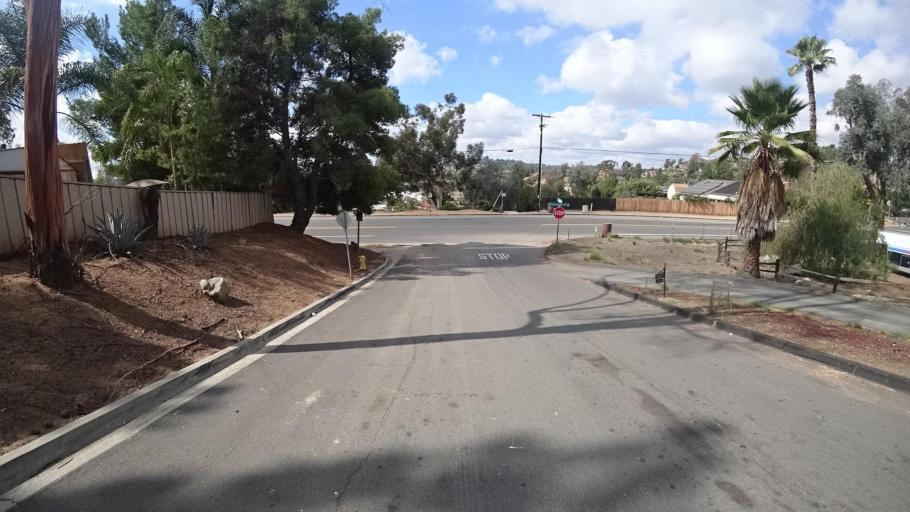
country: US
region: California
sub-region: San Diego County
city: Rancho San Diego
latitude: 32.7657
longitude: -116.9146
